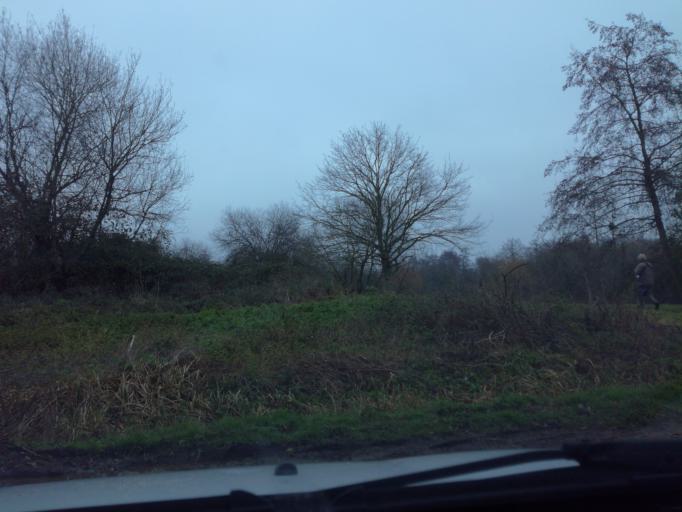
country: FR
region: Brittany
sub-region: Departement d'Ille-et-Vilaine
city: Saint-Jacques-de-la-Lande
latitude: 48.0772
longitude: -1.7559
